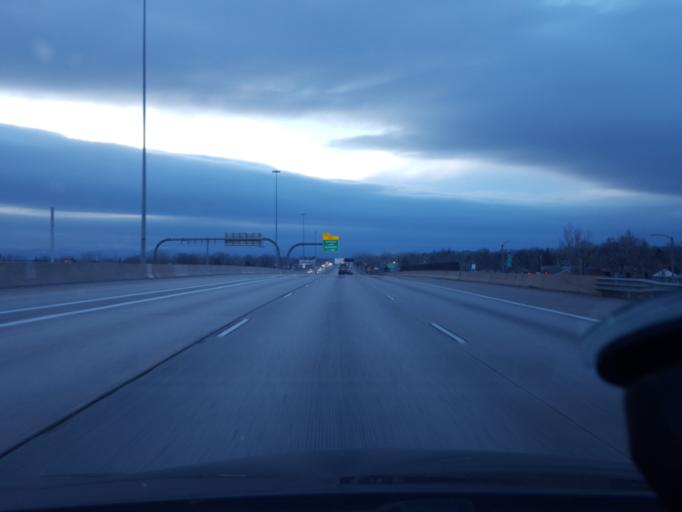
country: US
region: Colorado
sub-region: Adams County
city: Twin Lakes
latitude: 39.8305
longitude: -105.0048
